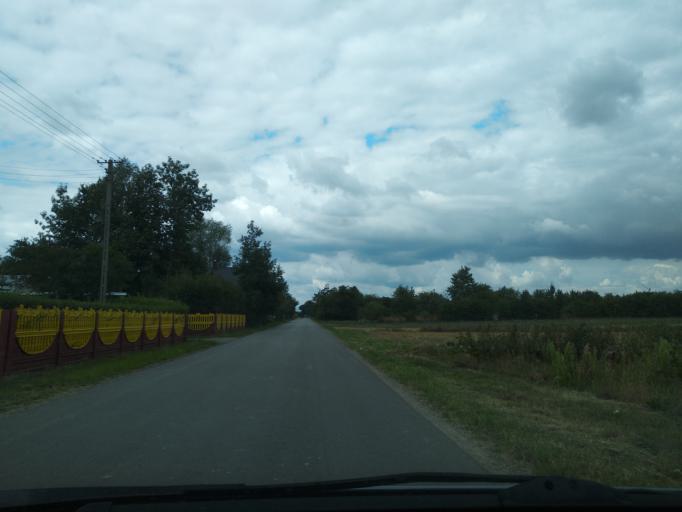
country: PL
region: Lublin Voivodeship
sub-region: Powiat lubartowski
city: Michow
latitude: 51.4959
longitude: 22.2872
